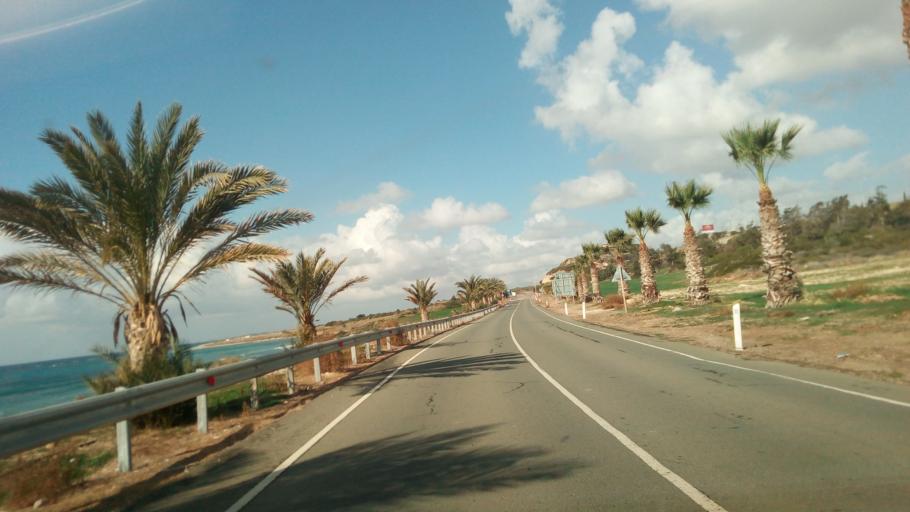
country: CY
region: Limassol
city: Pissouri
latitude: 34.6846
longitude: 32.5867
